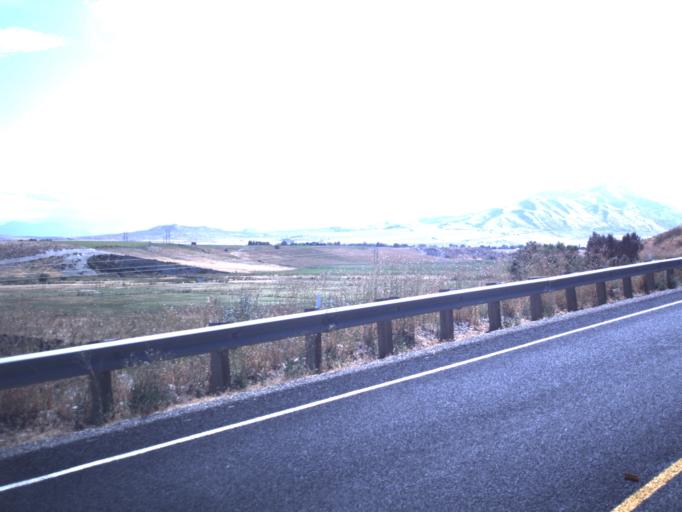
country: US
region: Utah
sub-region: Box Elder County
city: Garland
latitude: 41.8329
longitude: -112.1462
